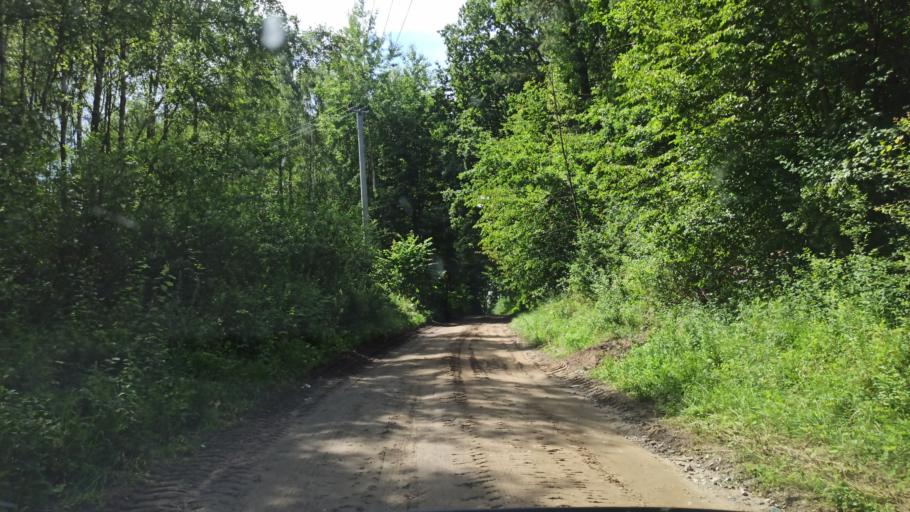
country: PL
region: Warmian-Masurian Voivodeship
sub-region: Powiat ostrodzki
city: Morag
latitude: 53.8659
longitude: 20.0437
